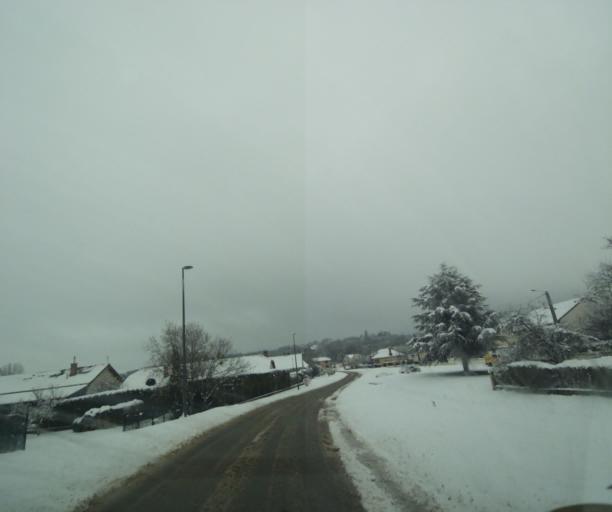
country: FR
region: Champagne-Ardenne
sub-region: Departement de la Haute-Marne
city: Wassy
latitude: 48.5639
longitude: 4.8956
